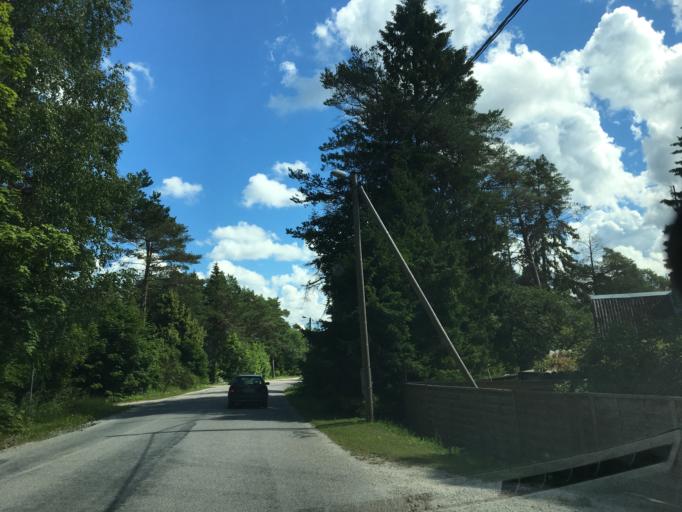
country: EE
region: Harju
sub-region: Nissi vald
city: Riisipere
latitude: 59.2430
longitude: 24.2949
